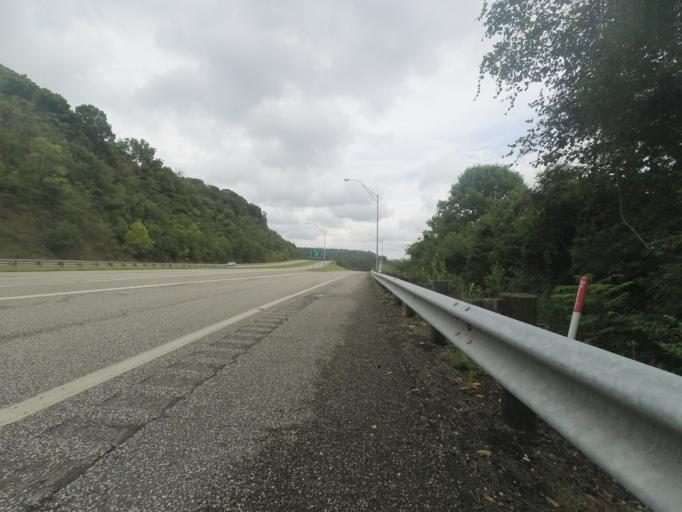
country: US
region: West Virginia
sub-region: Cabell County
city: Huntington
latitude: 38.4278
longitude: -82.4683
